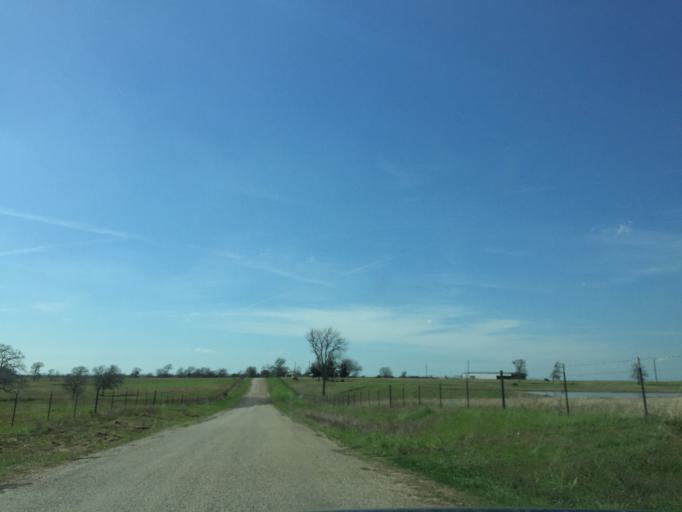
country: US
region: Texas
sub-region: Milam County
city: Thorndale
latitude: 30.5769
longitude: -97.1724
